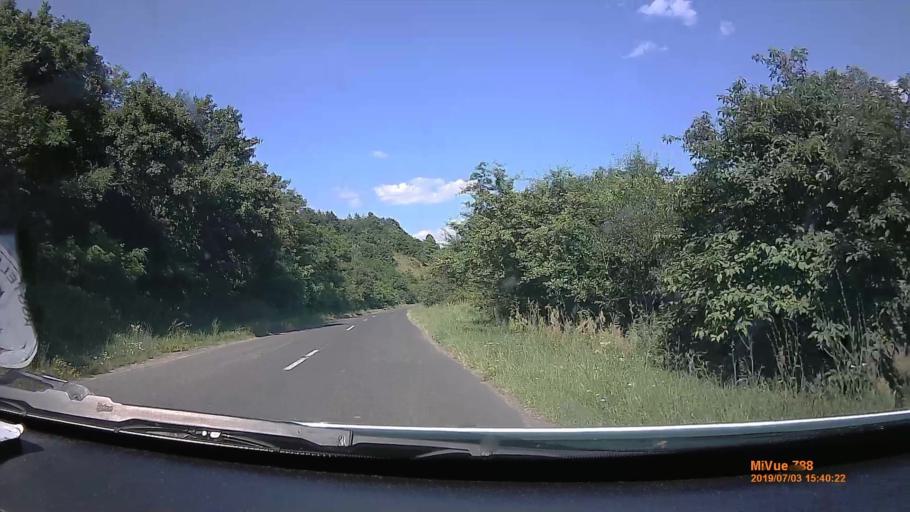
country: HU
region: Heves
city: Szilvasvarad
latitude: 48.1650
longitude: 20.4106
